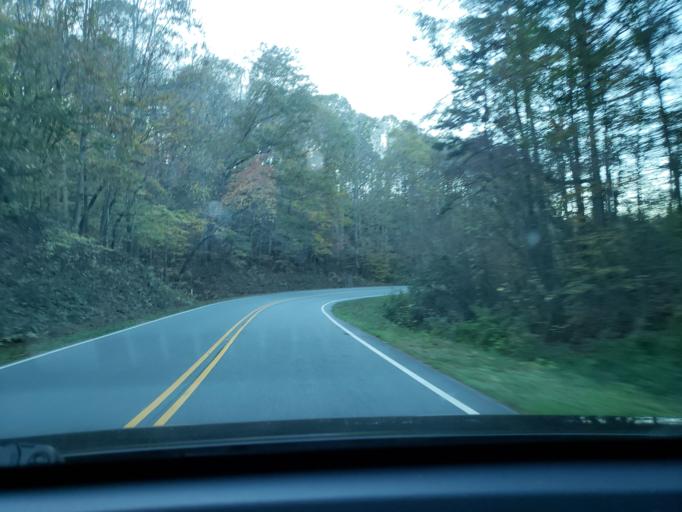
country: US
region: North Carolina
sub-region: Stokes County
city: Danbury
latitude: 36.3867
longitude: -80.1901
